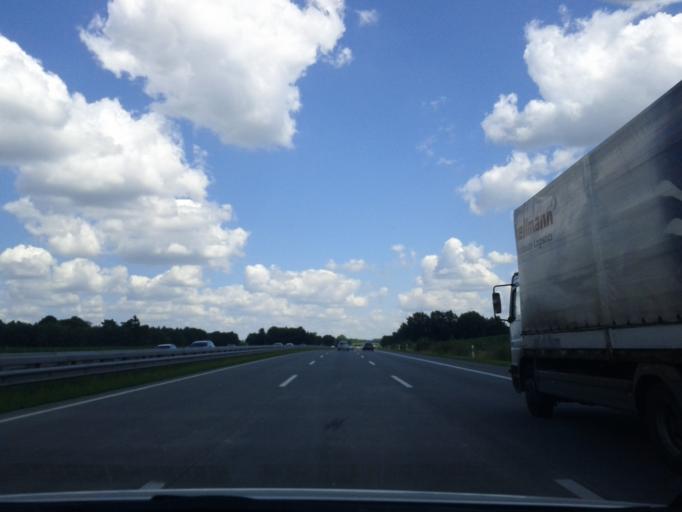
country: DE
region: Lower Saxony
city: Horstedt
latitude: 53.1585
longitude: 9.2383
